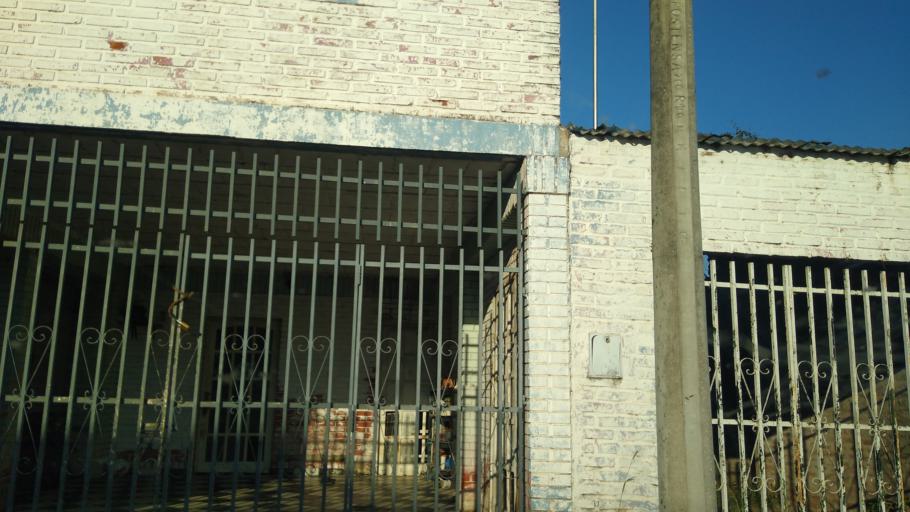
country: AR
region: Chaco
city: Barranqueras
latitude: -27.4784
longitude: -58.9464
